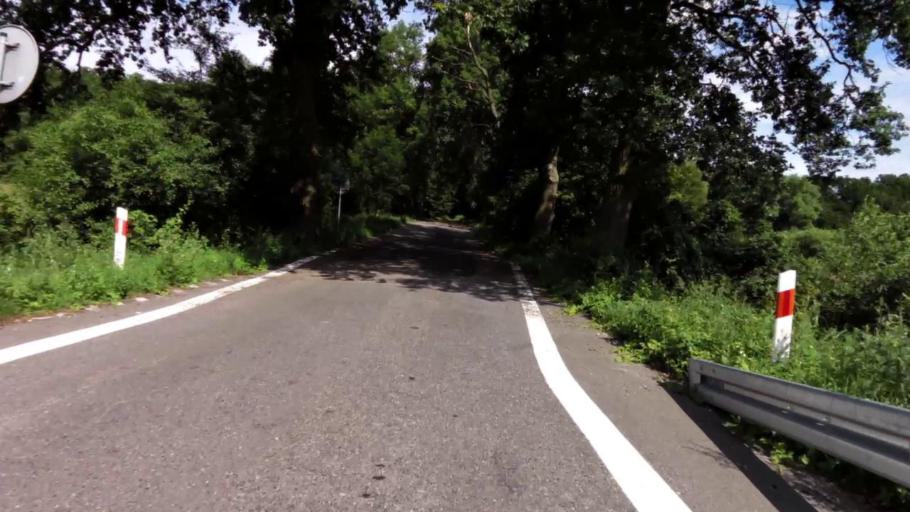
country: PL
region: West Pomeranian Voivodeship
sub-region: Powiat stargardzki
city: Dobrzany
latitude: 53.3864
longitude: 15.4504
